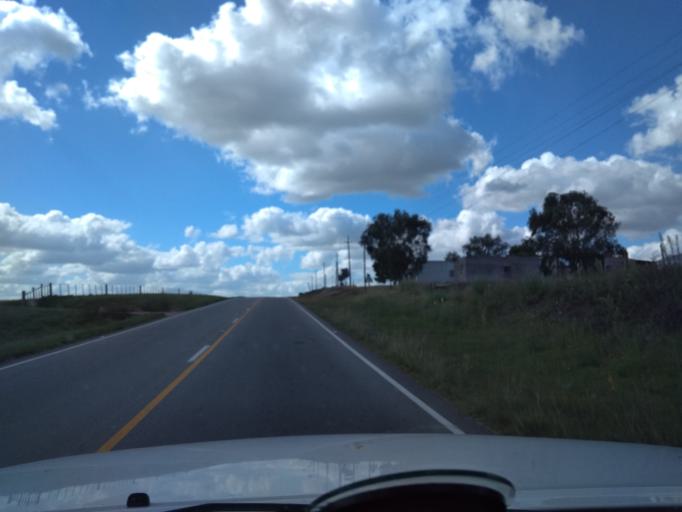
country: UY
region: Canelones
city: Joaquin Suarez
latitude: -34.7040
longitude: -56.0578
